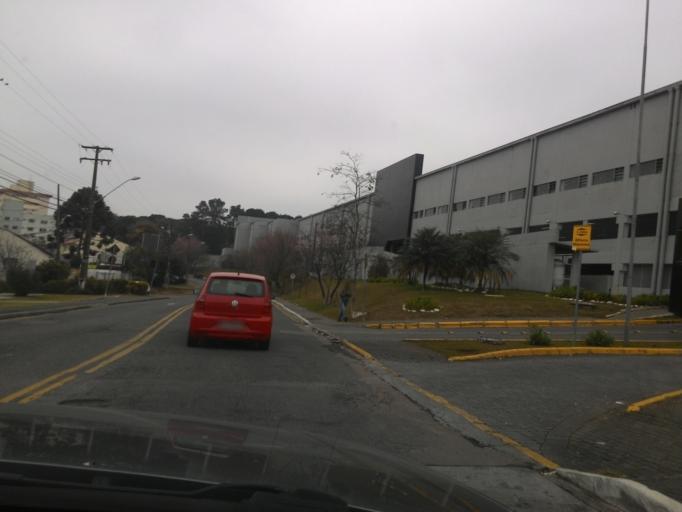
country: BR
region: Parana
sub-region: Curitiba
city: Curitiba
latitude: -25.4783
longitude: -49.2873
